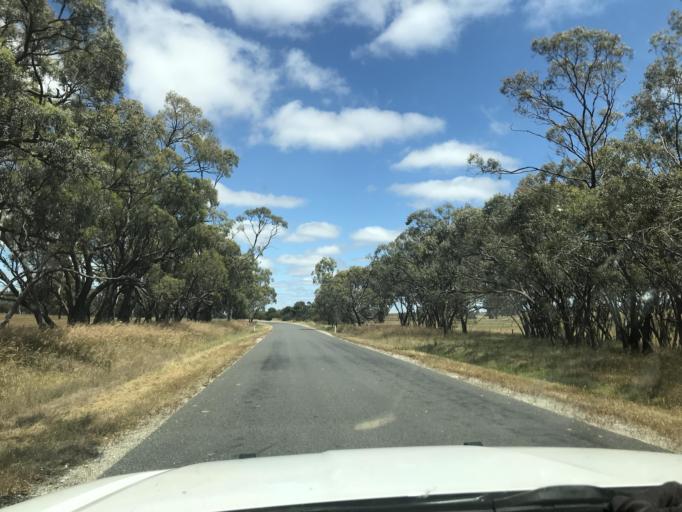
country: AU
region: South Australia
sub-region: Tatiara
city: Bordertown
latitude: -36.3108
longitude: 141.0247
